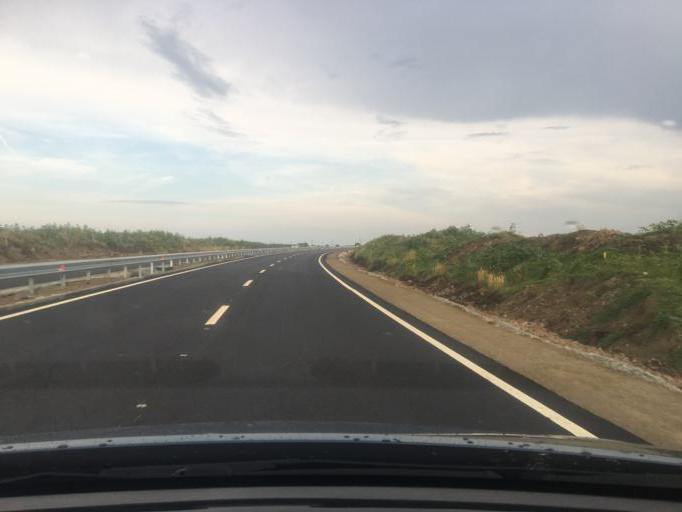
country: BG
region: Burgas
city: Aheloy
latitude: 42.6556
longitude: 27.6584
